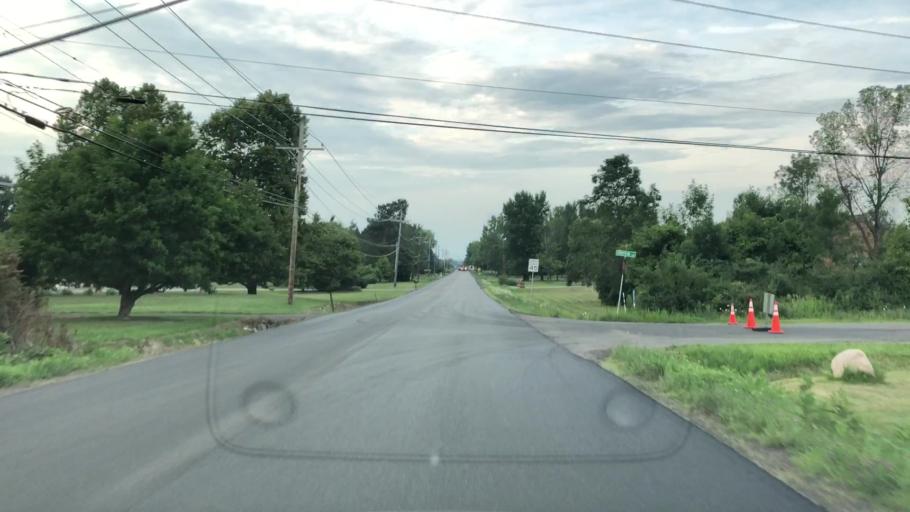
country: US
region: New York
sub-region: Erie County
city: Elma Center
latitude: 42.8181
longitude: -78.6059
